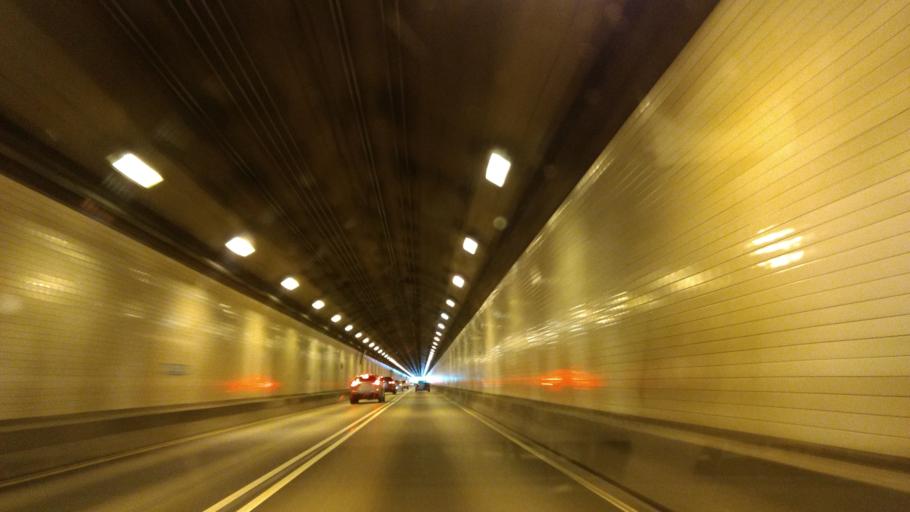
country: US
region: Pennsylvania
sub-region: Allegheny County
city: Homestead
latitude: 40.4267
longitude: -79.9182
